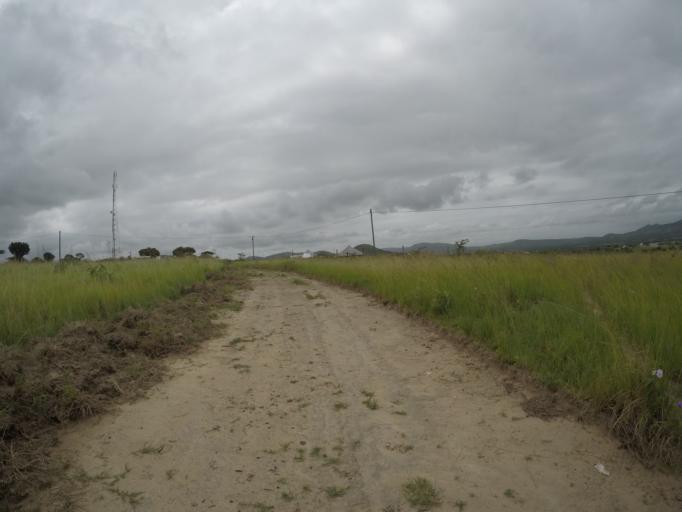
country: ZA
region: KwaZulu-Natal
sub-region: uThungulu District Municipality
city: Empangeni
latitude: -28.6059
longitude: 31.8344
